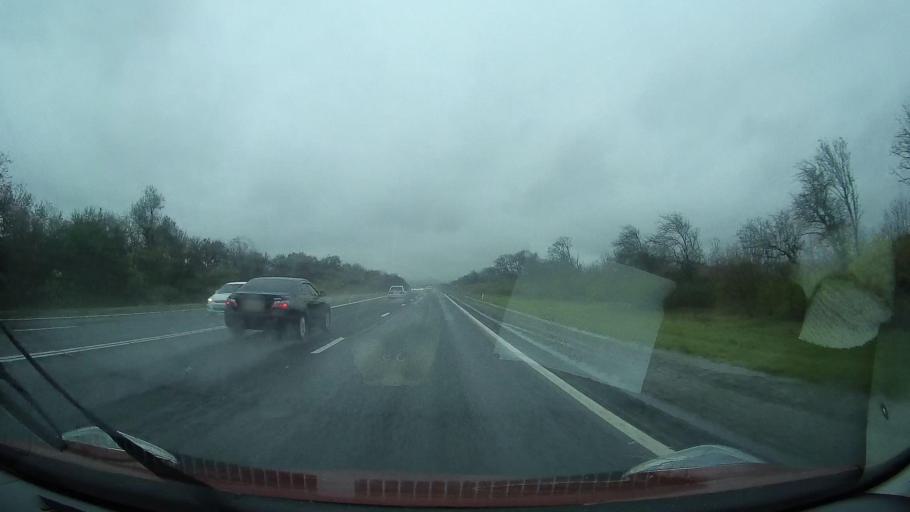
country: RU
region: Stavropol'skiy
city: Nevinnomyssk
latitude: 44.6177
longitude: 42.0999
